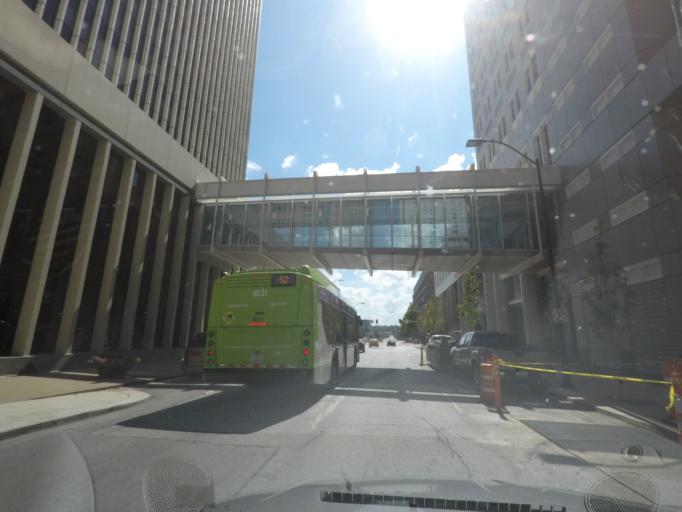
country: US
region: Iowa
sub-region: Polk County
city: Des Moines
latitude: 41.5861
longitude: -93.6261
